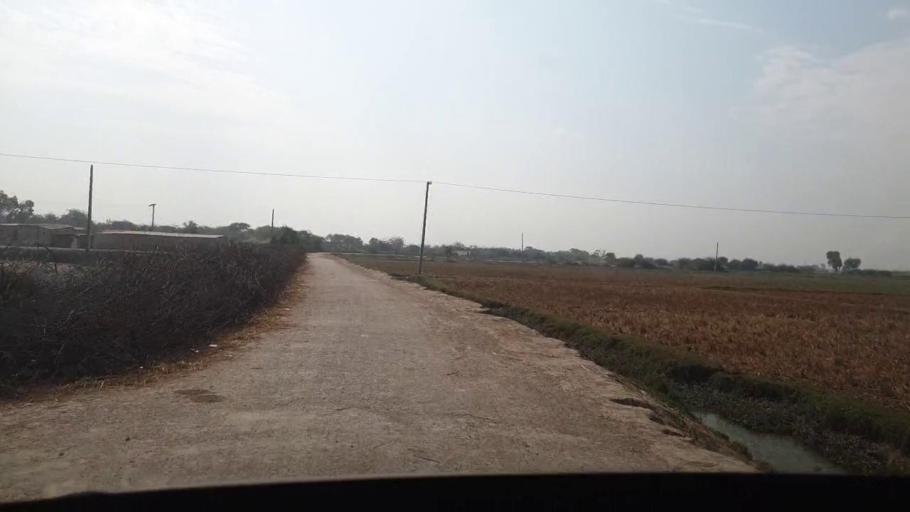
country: PK
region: Sindh
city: Chuhar Jamali
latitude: 24.3180
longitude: 67.9444
